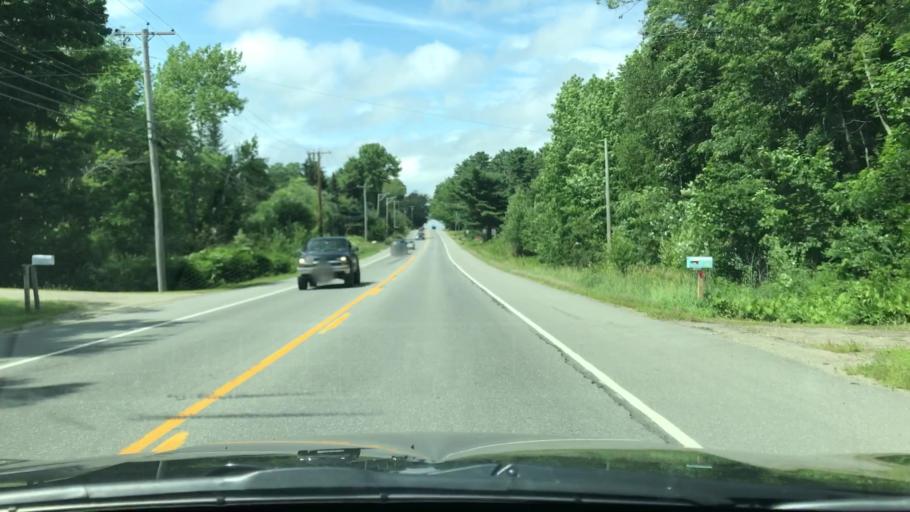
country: US
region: Maine
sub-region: Waldo County
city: Belfast
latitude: 44.3848
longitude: -68.9872
